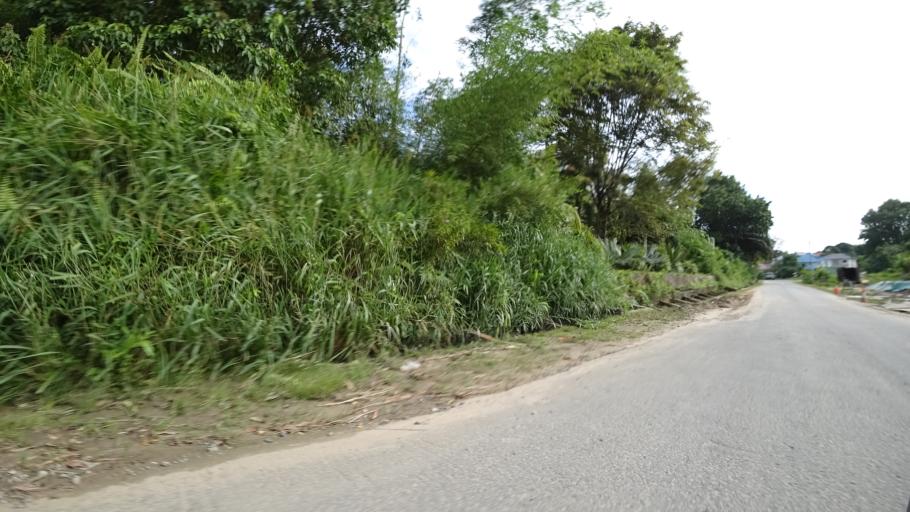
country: BN
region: Brunei and Muara
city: Bandar Seri Begawan
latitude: 4.8923
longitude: 114.9266
